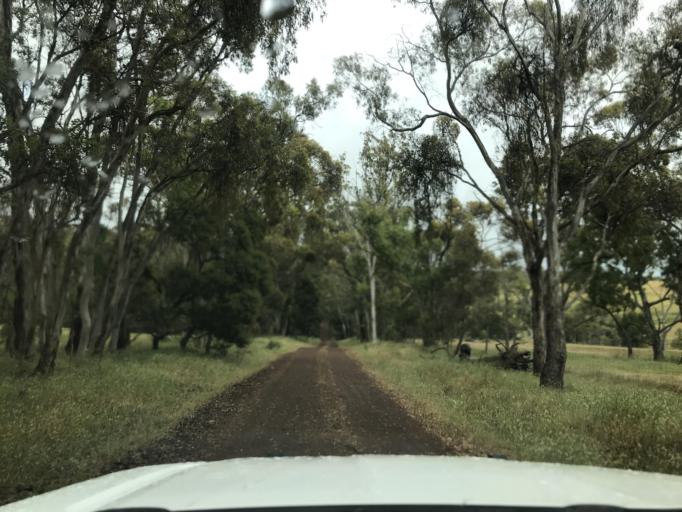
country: AU
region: South Australia
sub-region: Wattle Range
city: Penola
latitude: -37.2637
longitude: 141.3196
